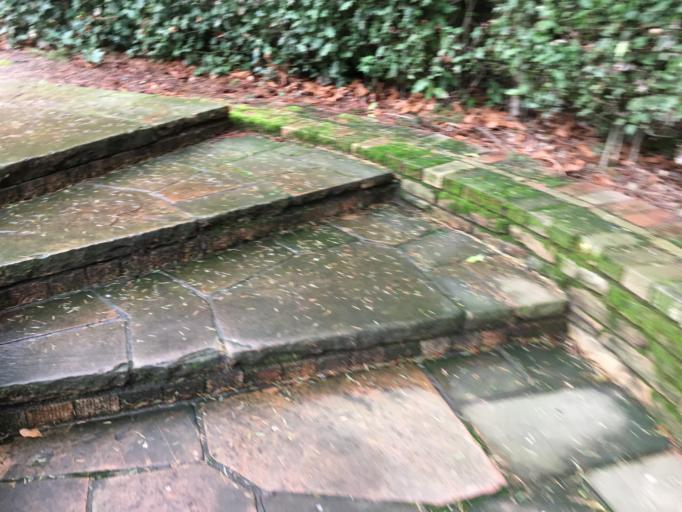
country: US
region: Washington
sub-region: King County
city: Seattle
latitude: 47.6608
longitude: -122.3072
